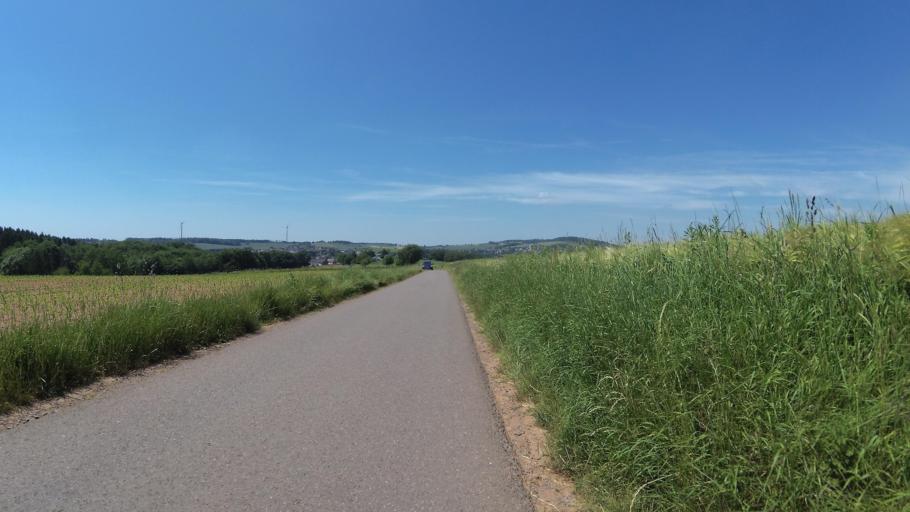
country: DE
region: Saarland
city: Eppelborn
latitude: 49.3972
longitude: 6.9375
